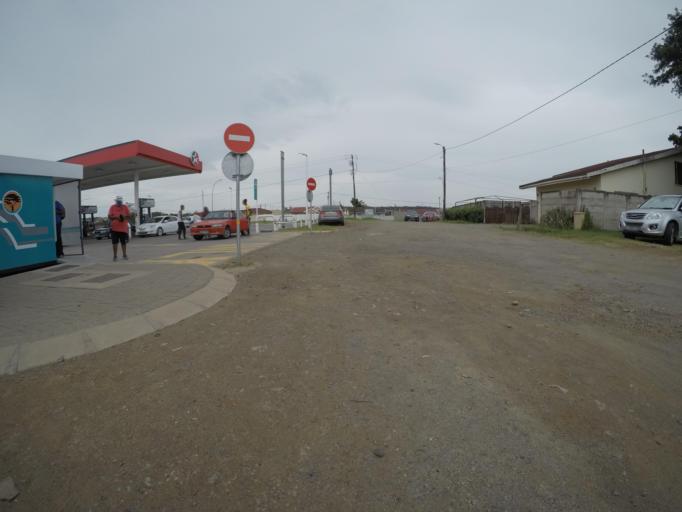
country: ZA
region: Eastern Cape
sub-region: Buffalo City Metropolitan Municipality
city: East London
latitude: -32.9976
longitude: 27.8478
